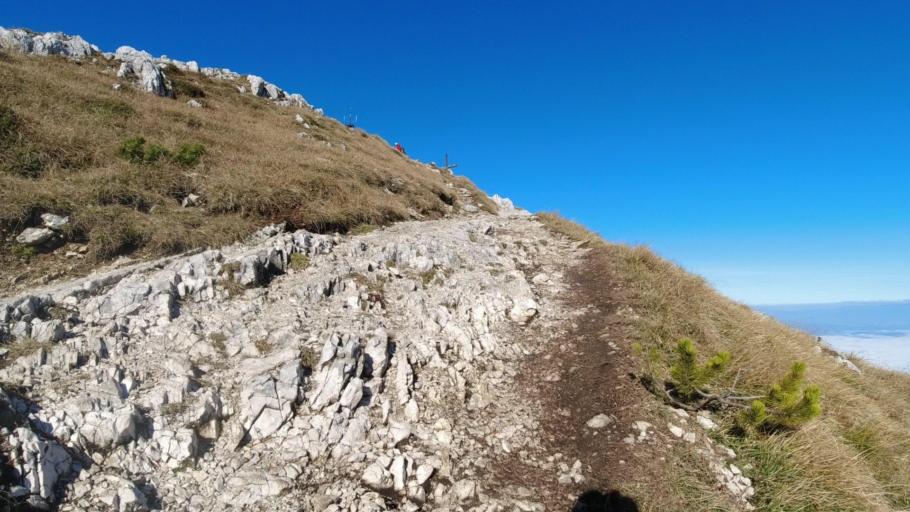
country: AT
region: Carinthia
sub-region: Politischer Bezirk Volkermarkt
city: Gallizien
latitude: 46.5057
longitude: 14.4872
